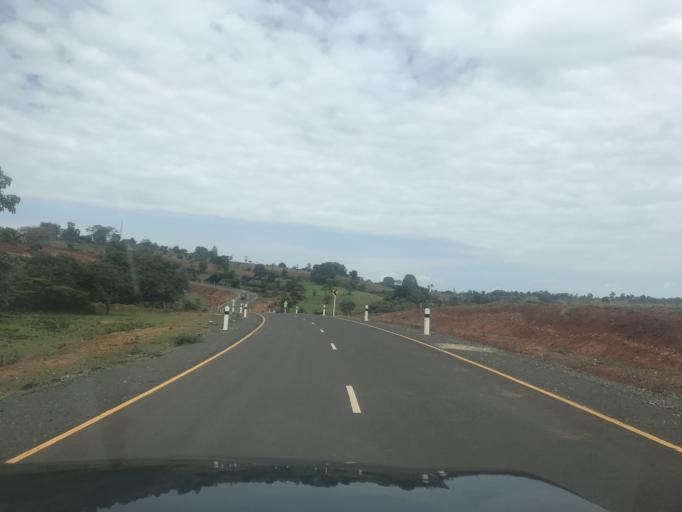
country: ET
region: Oromiya
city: Shambu
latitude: 9.8732
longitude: 36.6966
